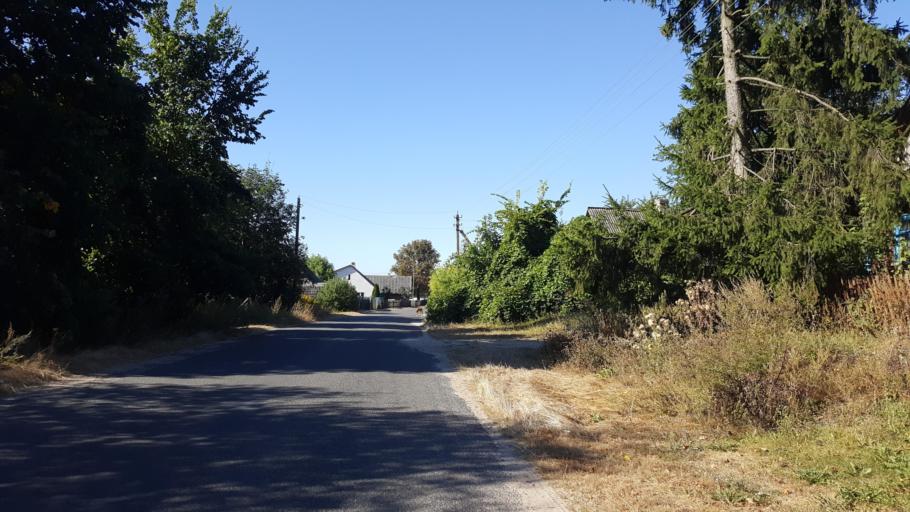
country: BY
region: Brest
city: Kamyanyets
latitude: 52.3785
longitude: 23.7403
